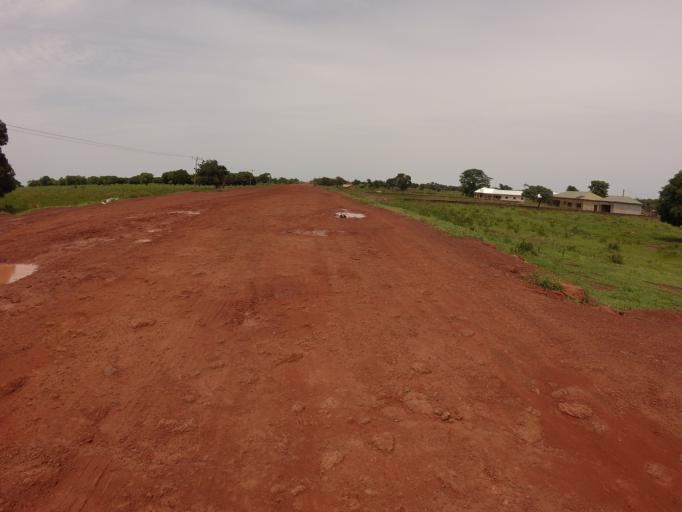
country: GH
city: Kpandae
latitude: 8.8385
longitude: 0.0607
